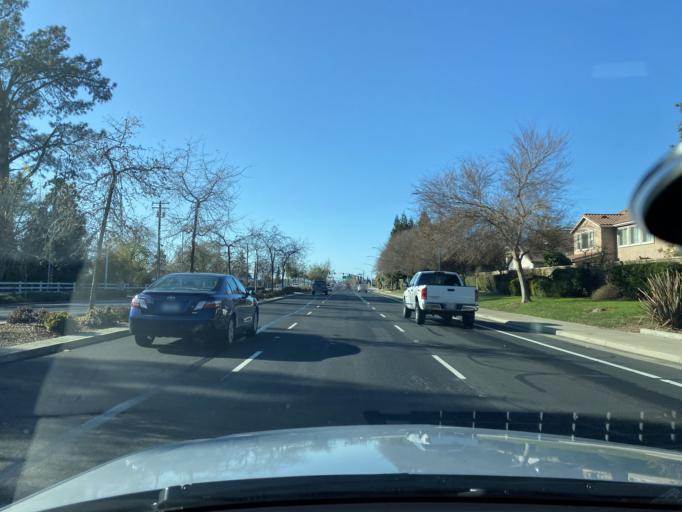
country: US
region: California
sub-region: Sacramento County
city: Laguna
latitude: 38.4381
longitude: -121.3941
